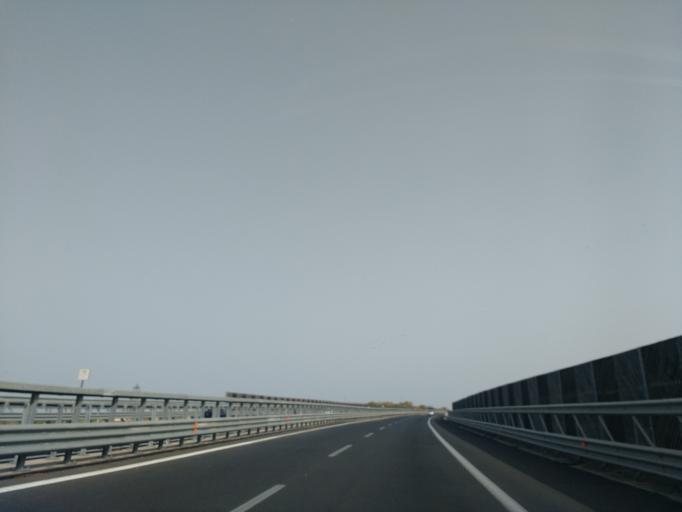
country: IT
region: Sicily
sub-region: Provincia di Siracusa
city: Villasmundo
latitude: 37.2821
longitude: 15.1194
